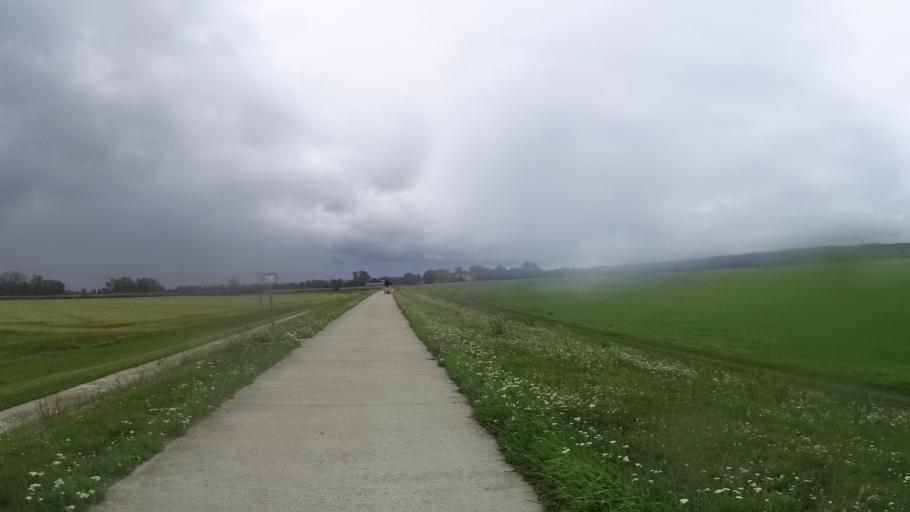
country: DE
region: Lower Saxony
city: Tosterglope
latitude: 53.2818
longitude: 10.8235
